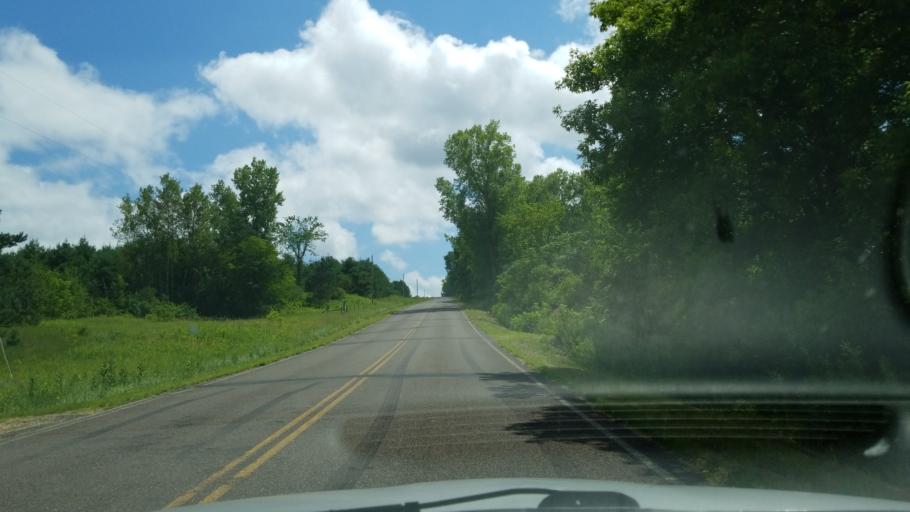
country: US
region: Wisconsin
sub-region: Saint Croix County
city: Glenwood City
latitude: 45.0352
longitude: -92.1773
